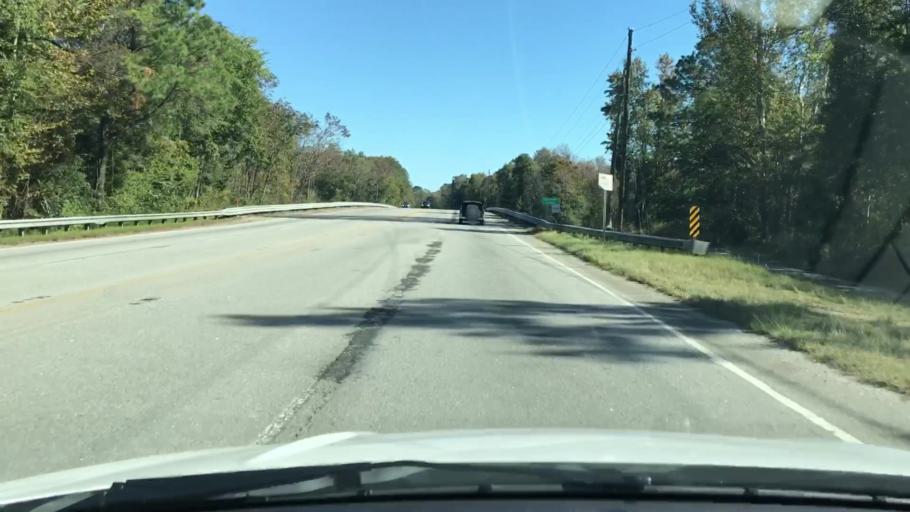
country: US
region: South Carolina
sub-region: Charleston County
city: Ravenel
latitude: 32.7656
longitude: -80.4478
